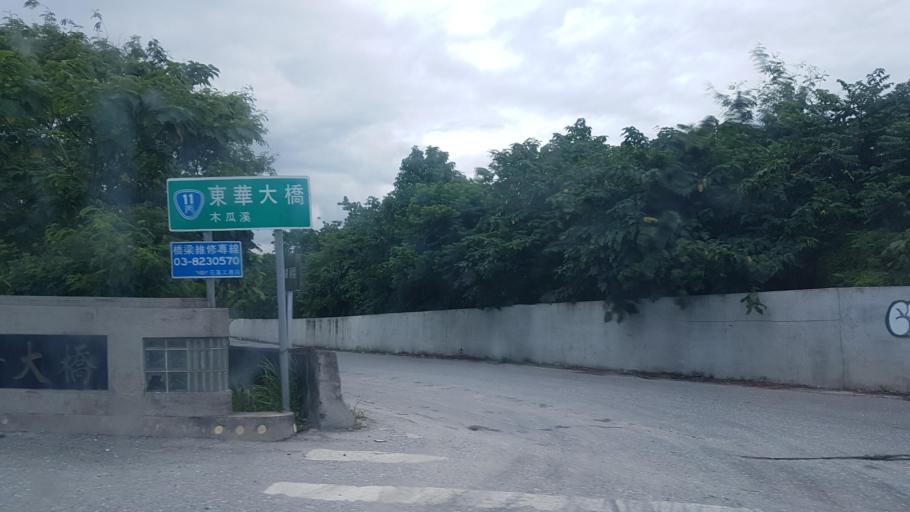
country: TW
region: Taiwan
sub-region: Hualien
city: Hualian
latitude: 23.9234
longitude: 121.5887
